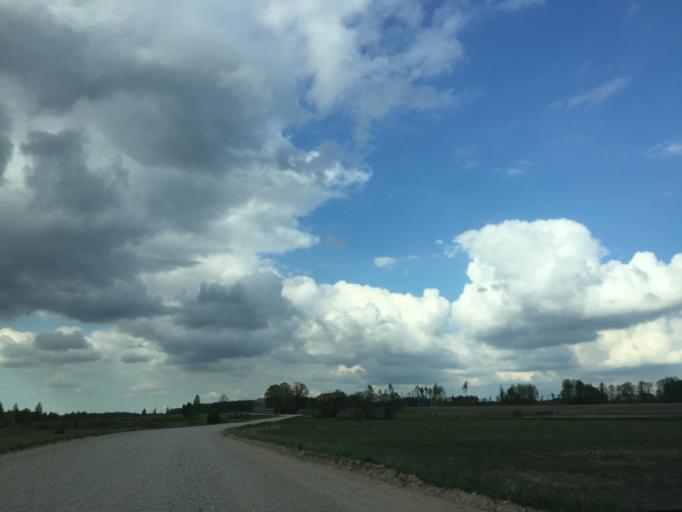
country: LV
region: Krimulda
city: Ragana
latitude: 57.3033
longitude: 24.7684
